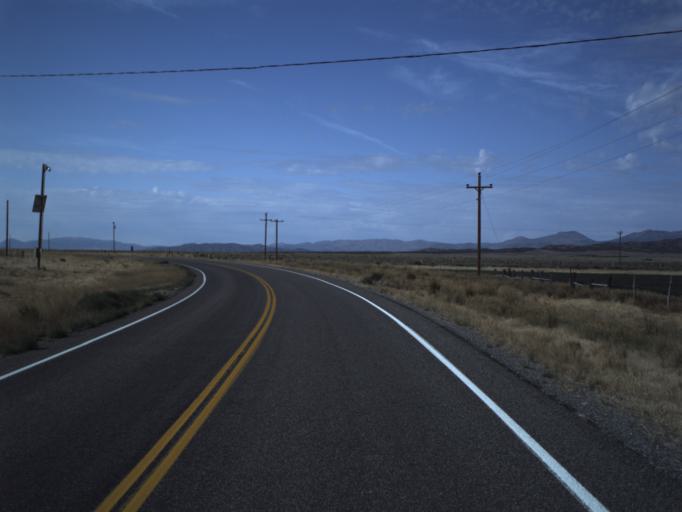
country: US
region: Idaho
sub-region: Cassia County
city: Burley
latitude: 41.7646
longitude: -113.5103
